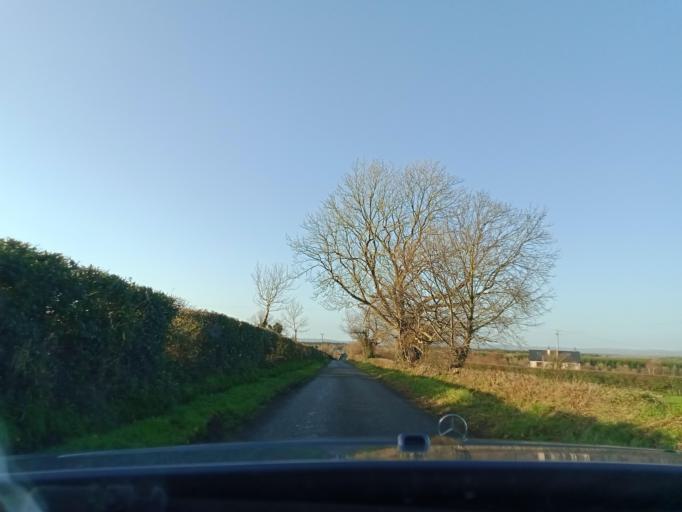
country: IE
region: Leinster
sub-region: Kilkenny
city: Callan
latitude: 52.5000
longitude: -7.3964
